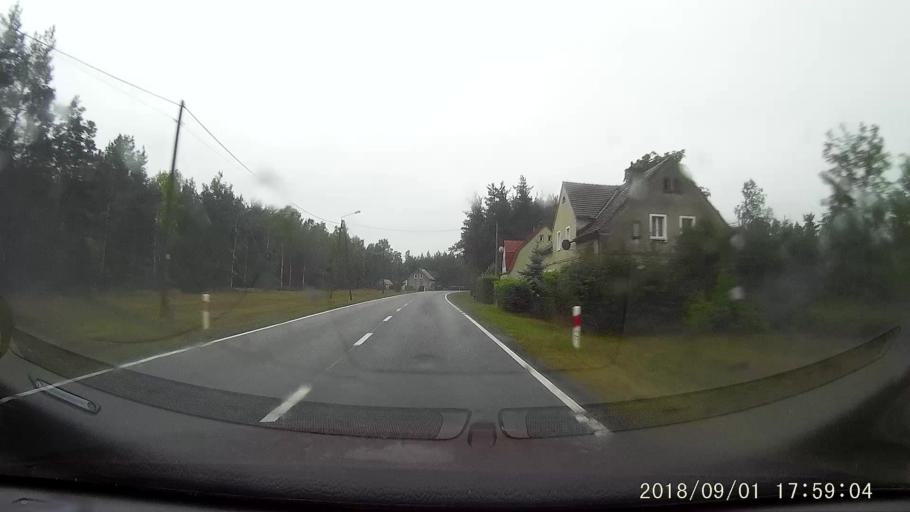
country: PL
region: Lubusz
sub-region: Powiat zaganski
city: Ilowa
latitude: 51.4124
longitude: 15.1852
